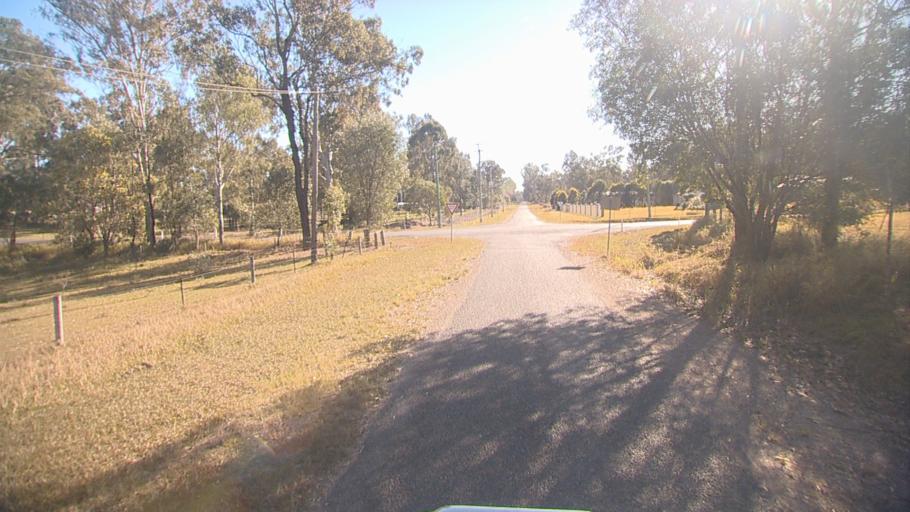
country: AU
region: Queensland
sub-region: Logan
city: North Maclean
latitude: -27.7588
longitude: 153.0331
